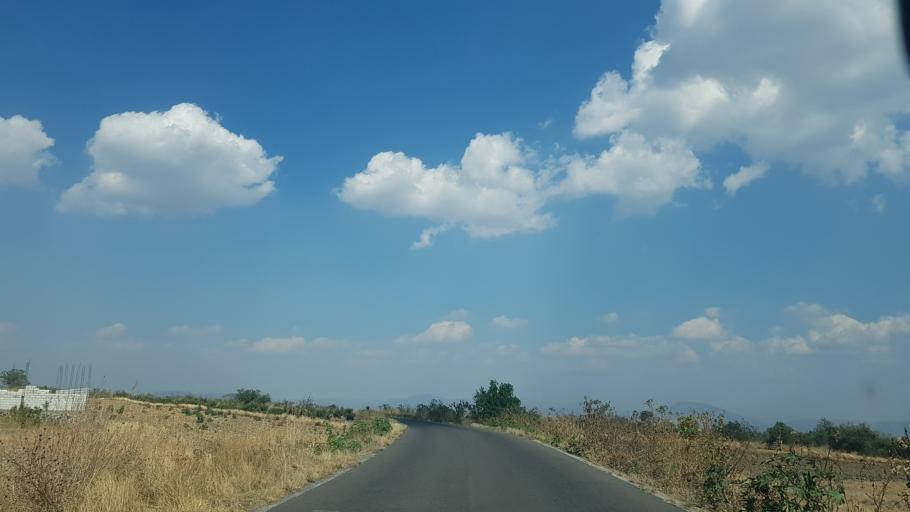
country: MX
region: Puebla
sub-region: Atlixco
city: Colonia Agricola de Ocotepec (Colonia San Jose)
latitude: 18.9178
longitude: -98.5274
